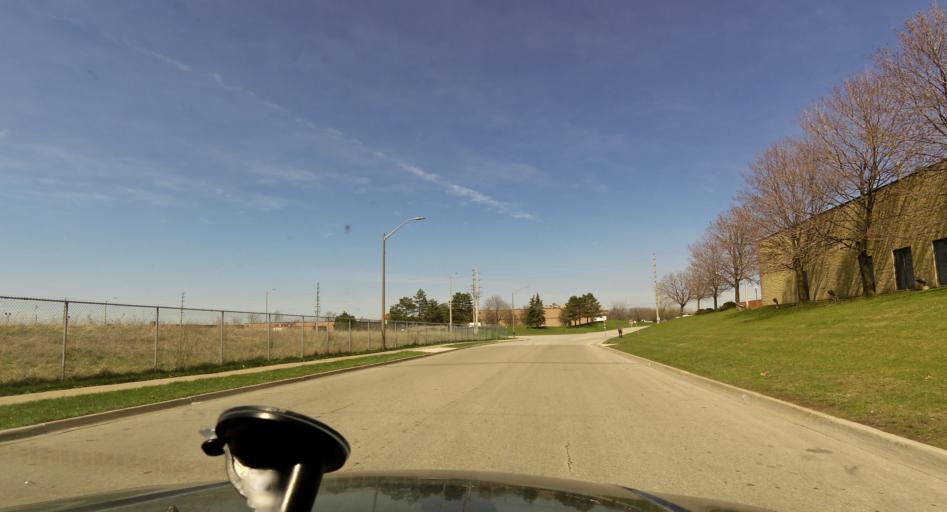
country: CA
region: Ontario
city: Etobicoke
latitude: 43.6452
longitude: -79.6179
